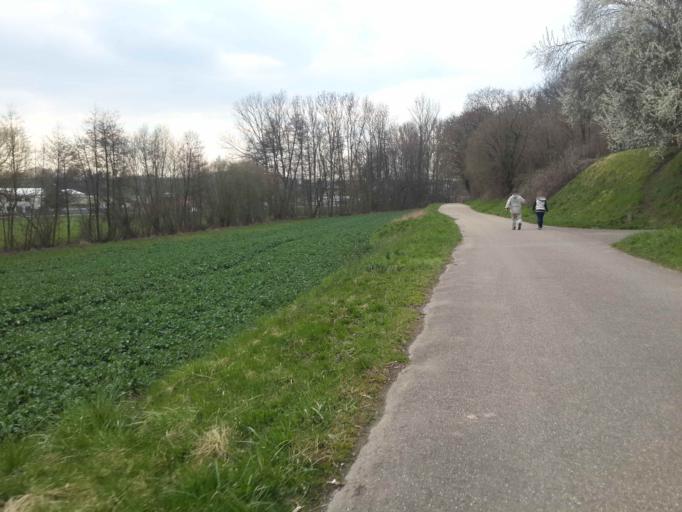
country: DE
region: Baden-Wuerttemberg
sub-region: Karlsruhe Region
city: Balzfeld
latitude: 49.2206
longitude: 8.7930
